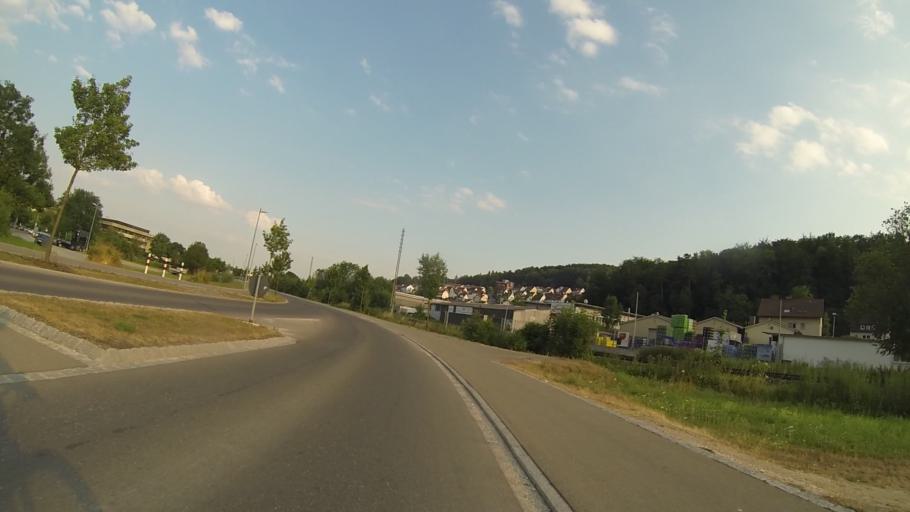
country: DE
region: Baden-Wuerttemberg
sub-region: Tuebingen Region
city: Dornstadt
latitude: 48.4173
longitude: 9.9148
